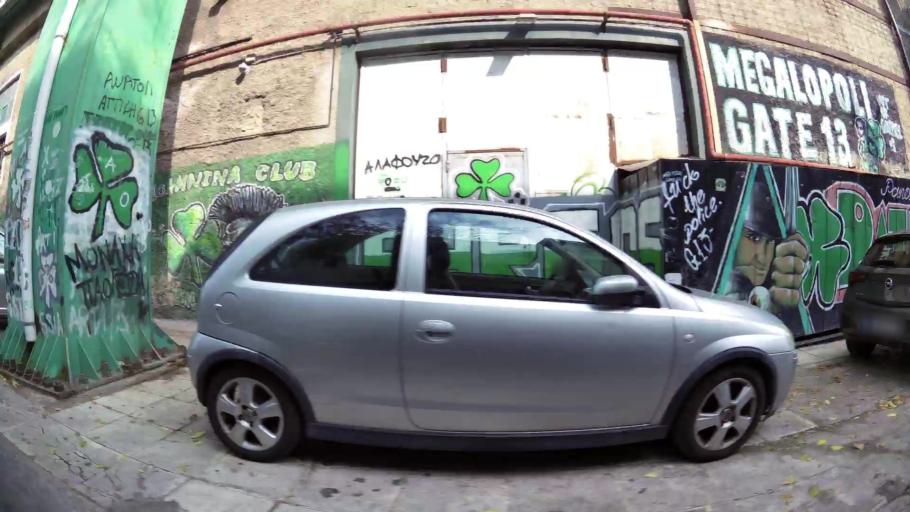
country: GR
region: Attica
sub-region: Nomarchia Athinas
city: Kipseli
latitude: 37.9866
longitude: 23.7546
